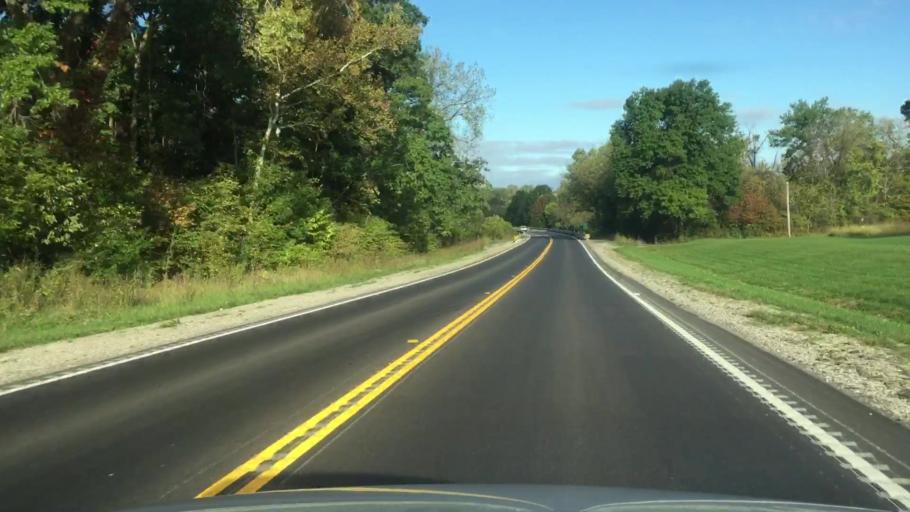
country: US
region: Missouri
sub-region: Howard County
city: New Franklin
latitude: 38.9918
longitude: -92.5627
